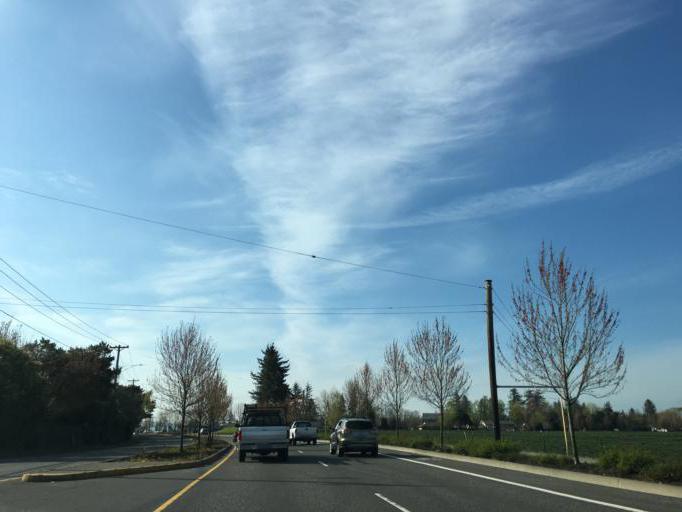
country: US
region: Oregon
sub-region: Multnomah County
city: Wood Village
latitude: 45.5227
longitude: -122.4133
